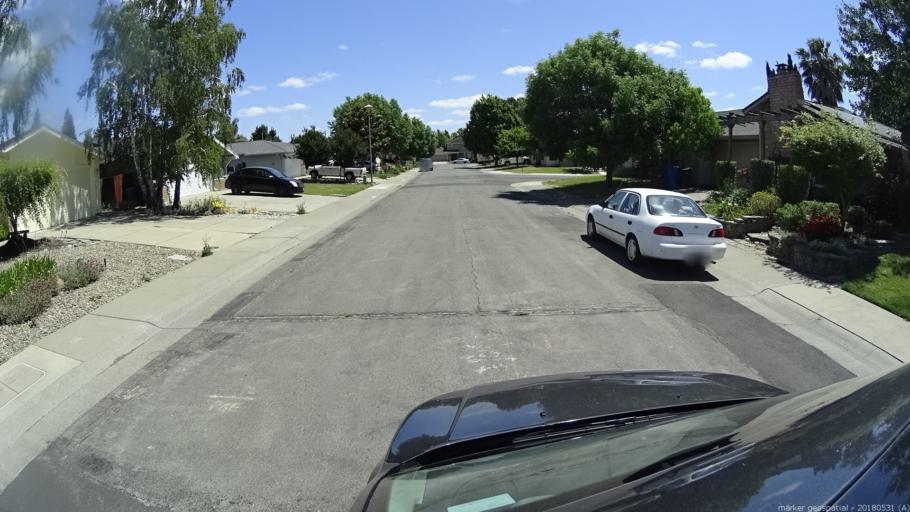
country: US
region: California
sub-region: Sacramento County
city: Sacramento
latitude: 38.6195
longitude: -121.5121
